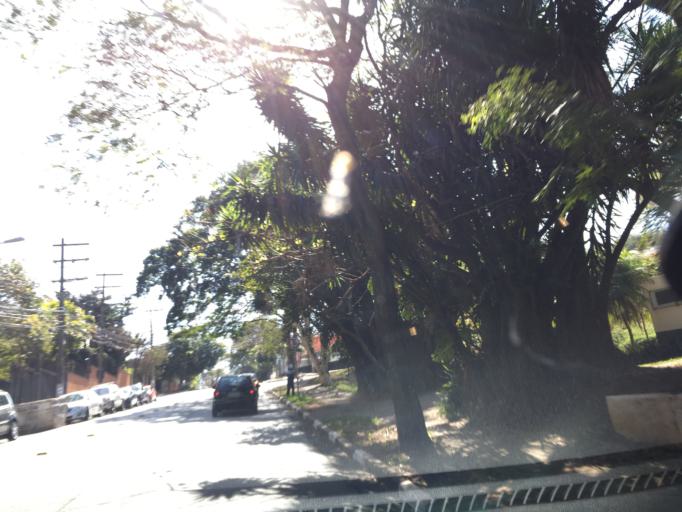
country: BR
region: Sao Paulo
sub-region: Sao Paulo
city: Sao Paulo
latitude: -23.5377
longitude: -46.7127
